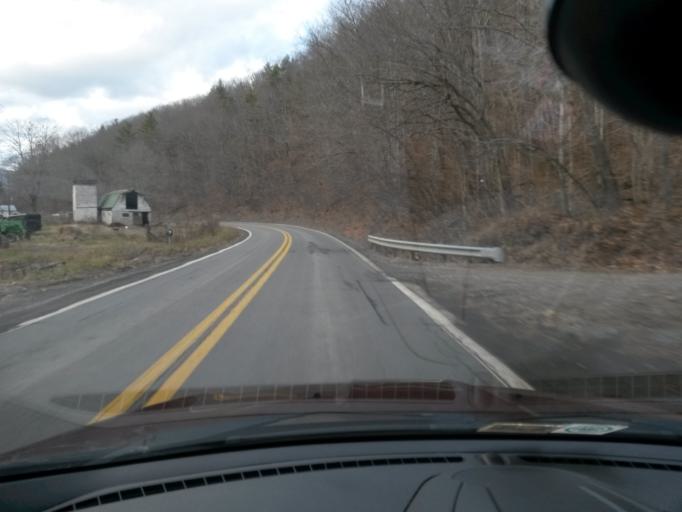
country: US
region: West Virginia
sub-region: Monroe County
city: Union
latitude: 37.5093
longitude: -80.6095
